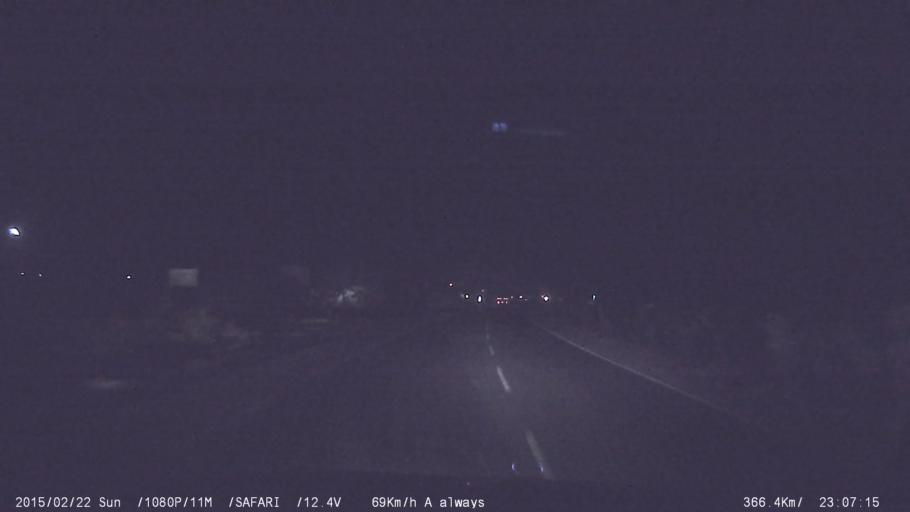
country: IN
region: Tamil Nadu
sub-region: Namakkal
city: Rasipuram
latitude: 11.4378
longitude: 78.1568
